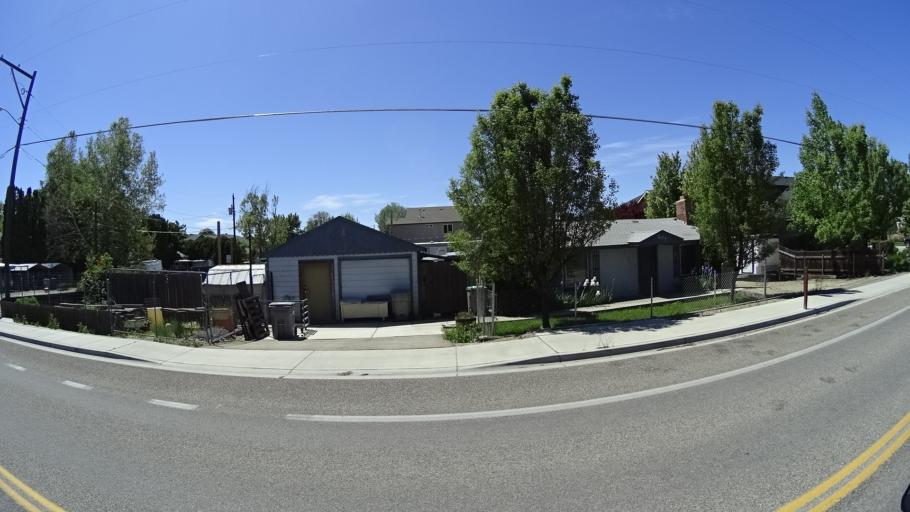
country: US
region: Idaho
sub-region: Ada County
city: Boise
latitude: 43.5861
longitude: -116.1782
